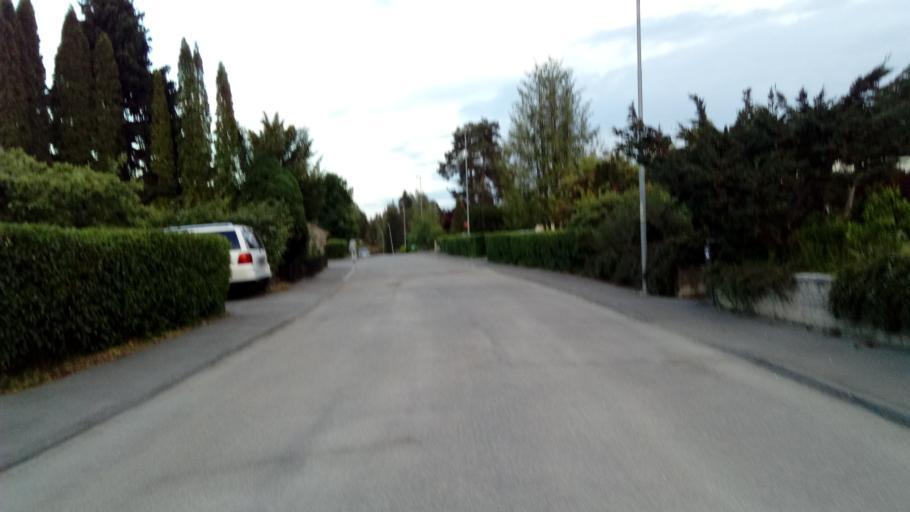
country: SE
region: Stockholm
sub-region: Tyreso Kommun
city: Bollmora
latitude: 59.2427
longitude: 18.2483
